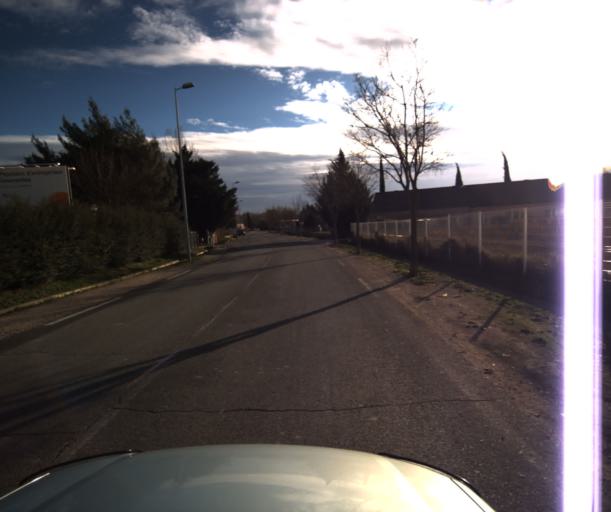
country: FR
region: Provence-Alpes-Cote d'Azur
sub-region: Departement du Vaucluse
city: Pertuis
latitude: 43.6755
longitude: 5.5029
